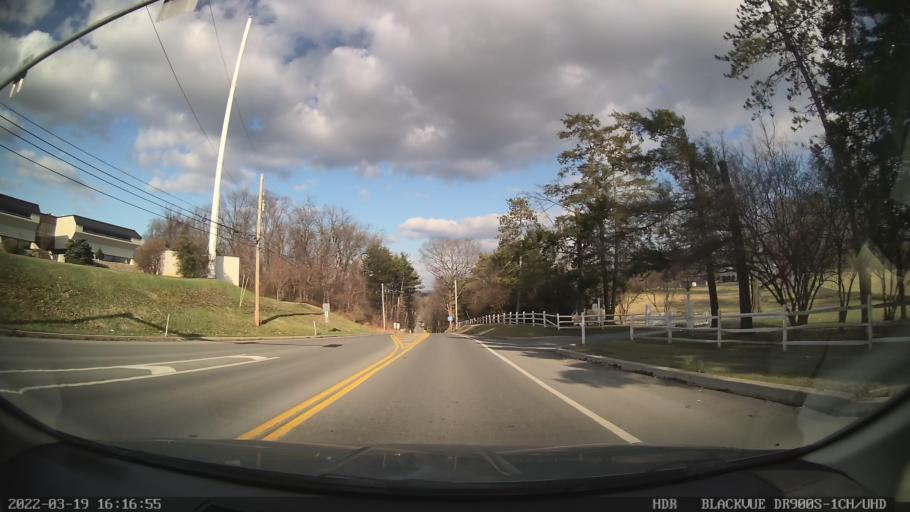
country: US
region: Pennsylvania
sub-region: Lehigh County
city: Dorneyville
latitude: 40.5622
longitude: -75.5172
